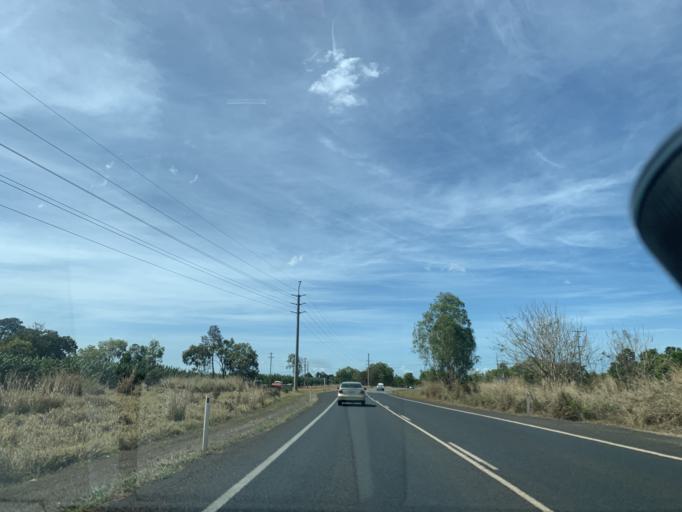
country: AU
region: Queensland
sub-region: Tablelands
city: Mareeba
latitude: -17.0864
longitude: 145.4352
